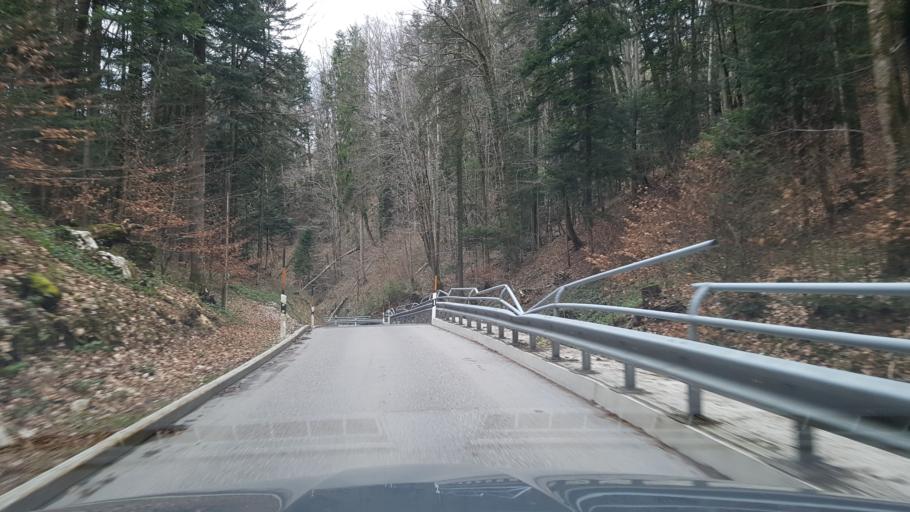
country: DE
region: Bavaria
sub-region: Upper Bavaria
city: Marktschellenberg
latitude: 47.6843
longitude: 13.0616
